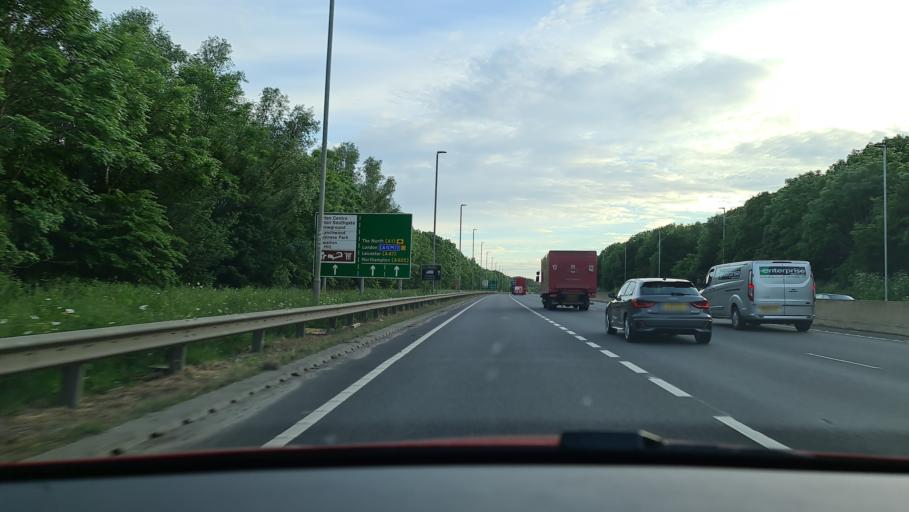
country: GB
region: England
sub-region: Cambridgeshire
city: Yaxley
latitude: 52.5391
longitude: -0.2900
